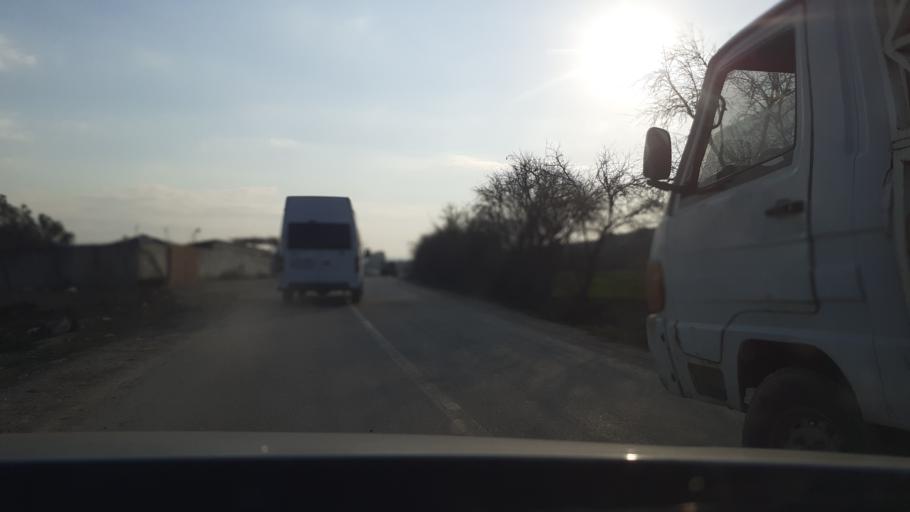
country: TR
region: Hatay
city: Boynuyogun
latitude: 36.1397
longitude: 36.3161
